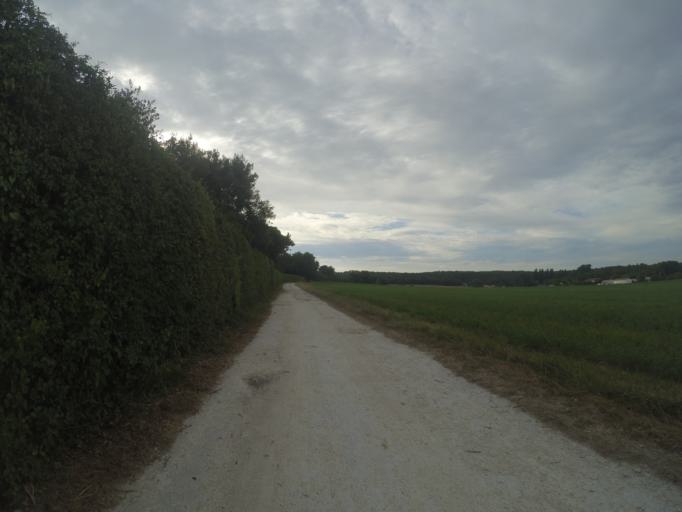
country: FR
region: Poitou-Charentes
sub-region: Departement de la Charente-Maritime
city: Meschers-sur-Gironde
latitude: 45.5736
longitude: -0.9685
